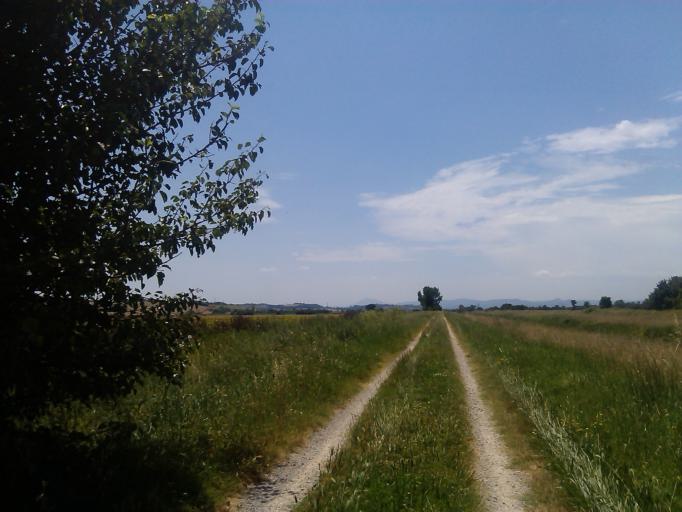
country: IT
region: Tuscany
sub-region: Province of Arezzo
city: Cesa
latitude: 43.2921
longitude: 11.8417
